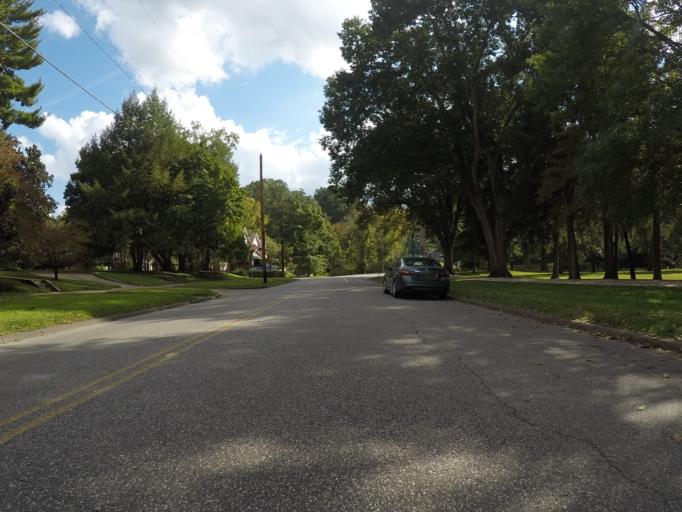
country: US
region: West Virginia
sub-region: Cabell County
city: Huntington
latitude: 38.4085
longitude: -82.4348
